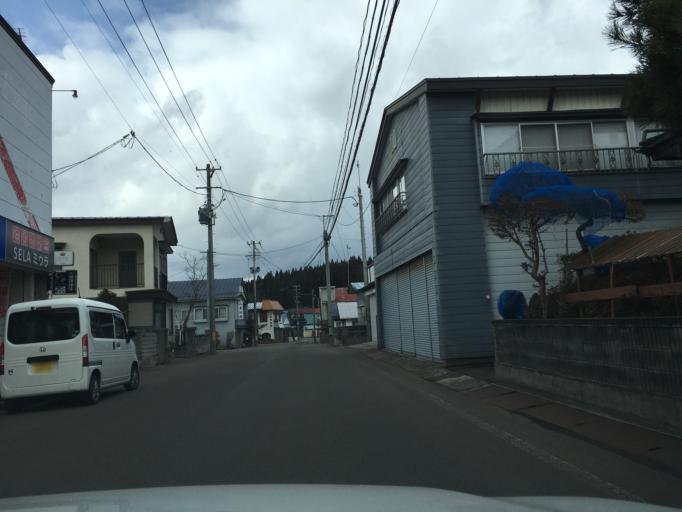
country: JP
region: Akita
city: Takanosu
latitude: 40.1613
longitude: 140.3294
